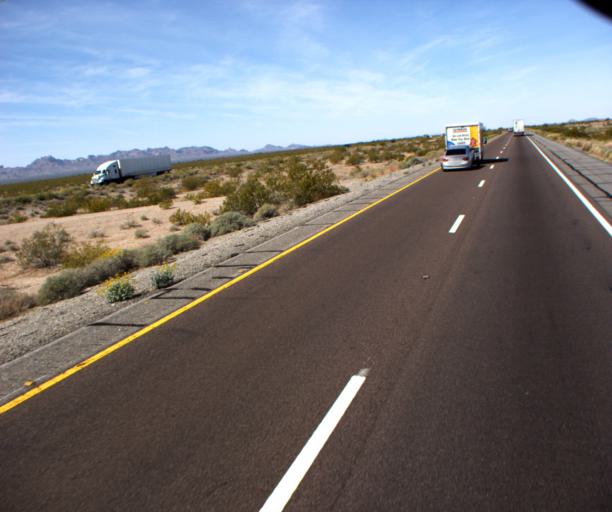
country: US
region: Arizona
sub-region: La Paz County
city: Salome
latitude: 33.5541
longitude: -113.2530
